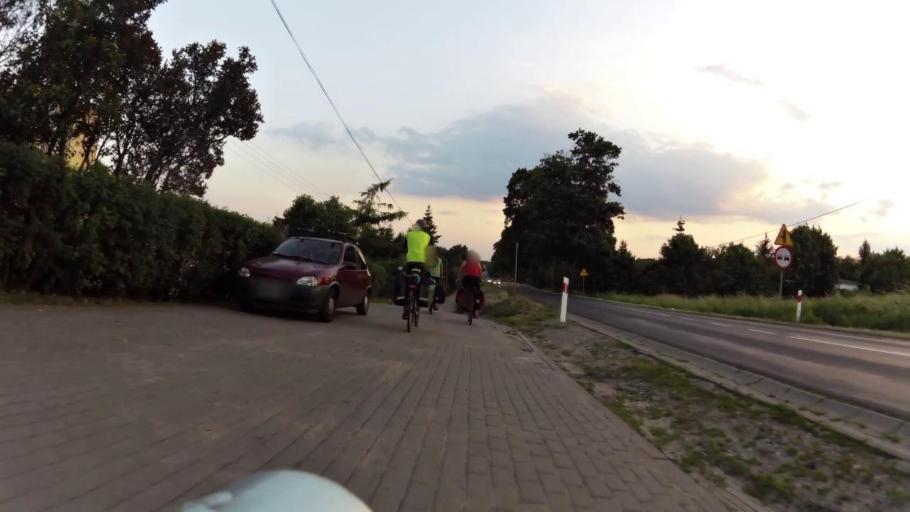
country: PL
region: Kujawsko-Pomorskie
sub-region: Bydgoszcz
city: Fordon
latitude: 53.1513
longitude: 18.2211
